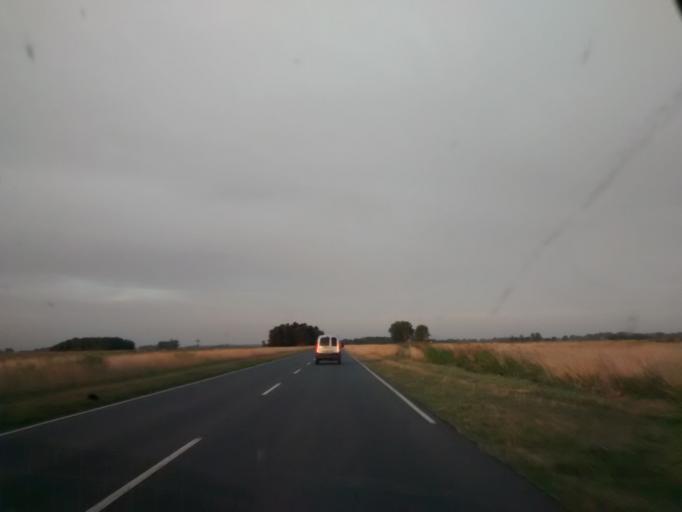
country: AR
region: Buenos Aires
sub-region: Partido de General Belgrano
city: General Belgrano
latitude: -35.8178
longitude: -58.5704
